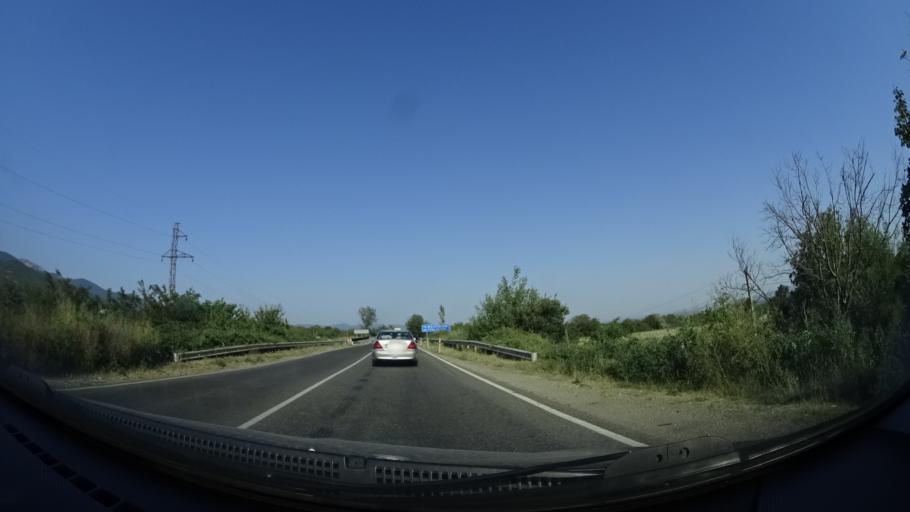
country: GE
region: Kakheti
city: Sagarejo
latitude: 41.7251
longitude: 45.3181
